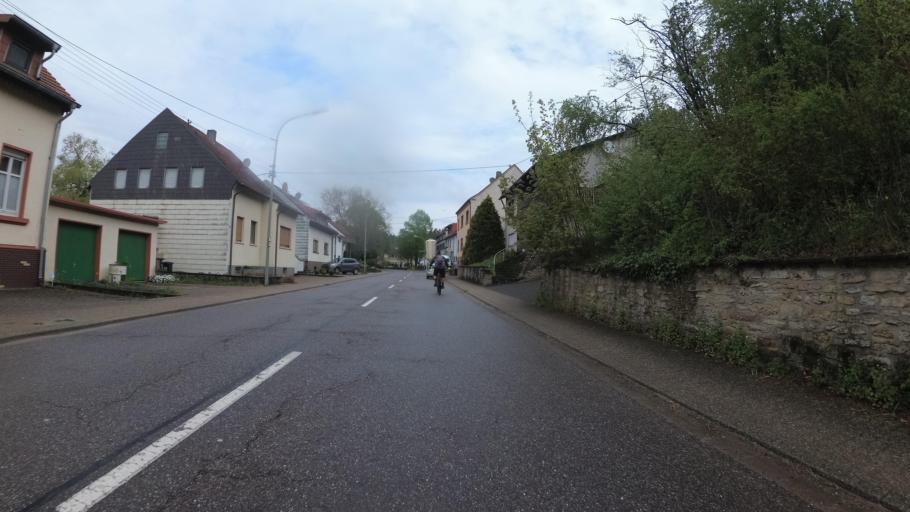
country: FR
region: Lorraine
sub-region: Departement de la Moselle
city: Bouzonville
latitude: 49.3413
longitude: 6.5943
